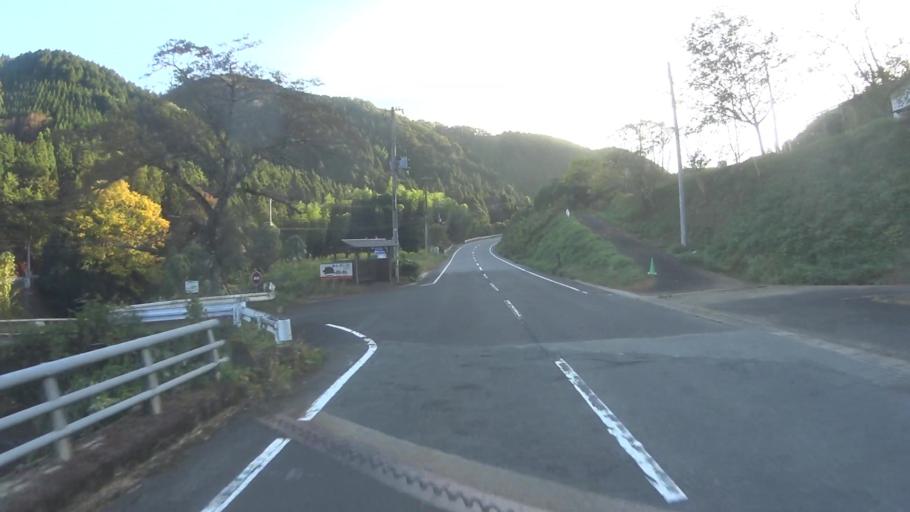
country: JP
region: Kyoto
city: Ayabe
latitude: 35.2287
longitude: 135.2443
